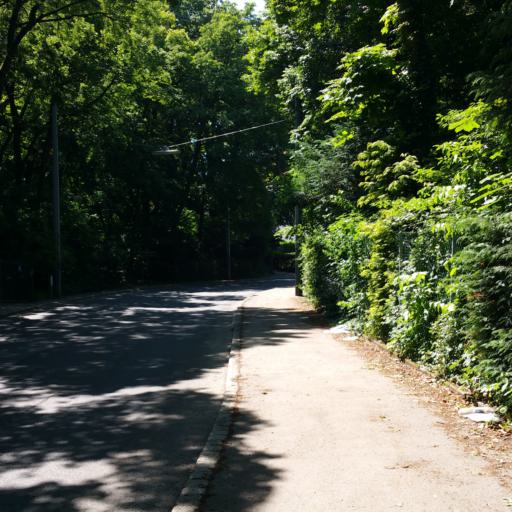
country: AT
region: Vienna
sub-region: Wien Stadt
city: Vienna
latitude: 48.2212
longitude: 16.2866
